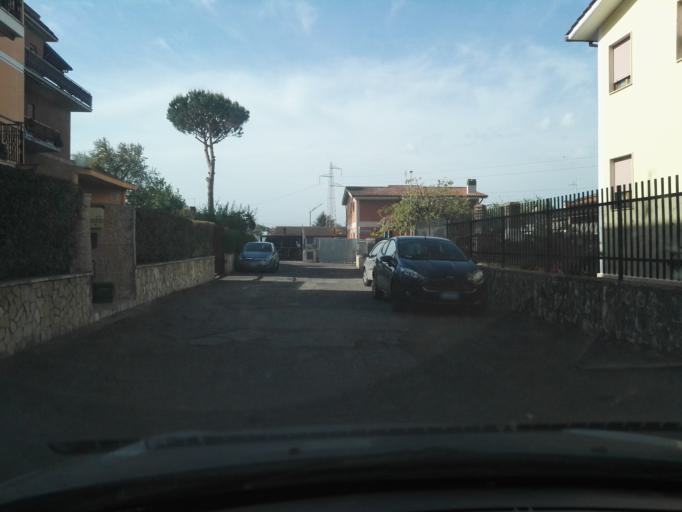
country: IT
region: Latium
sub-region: Citta metropolitana di Roma Capitale
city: Selcetta
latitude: 41.7702
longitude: 12.4822
